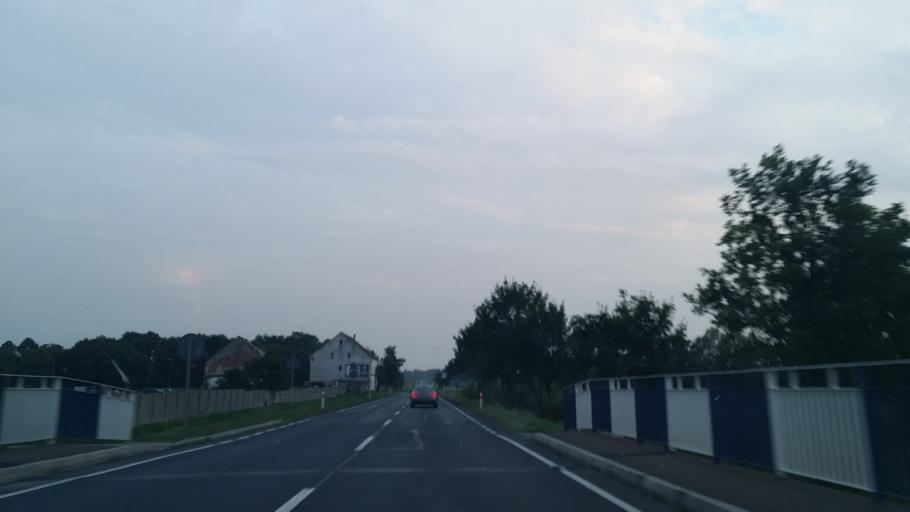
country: PL
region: Lower Silesian Voivodeship
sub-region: Powiat legnicki
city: Prochowice
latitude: 51.2873
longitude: 16.3471
